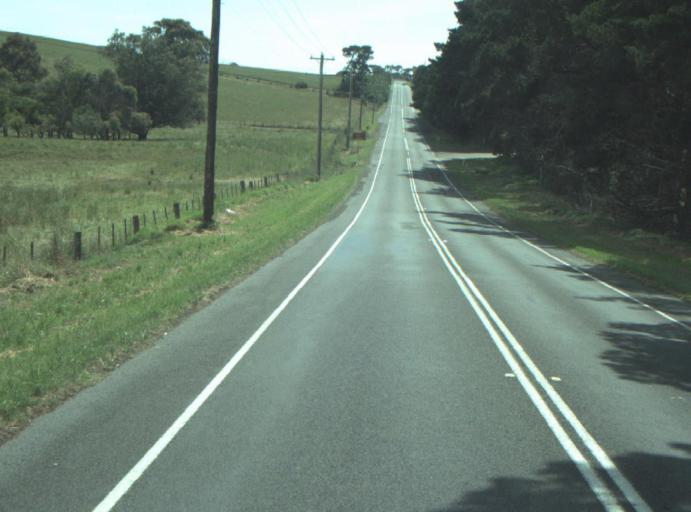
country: AU
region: Victoria
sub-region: Greater Geelong
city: Clifton Springs
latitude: -38.1489
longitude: 144.5944
